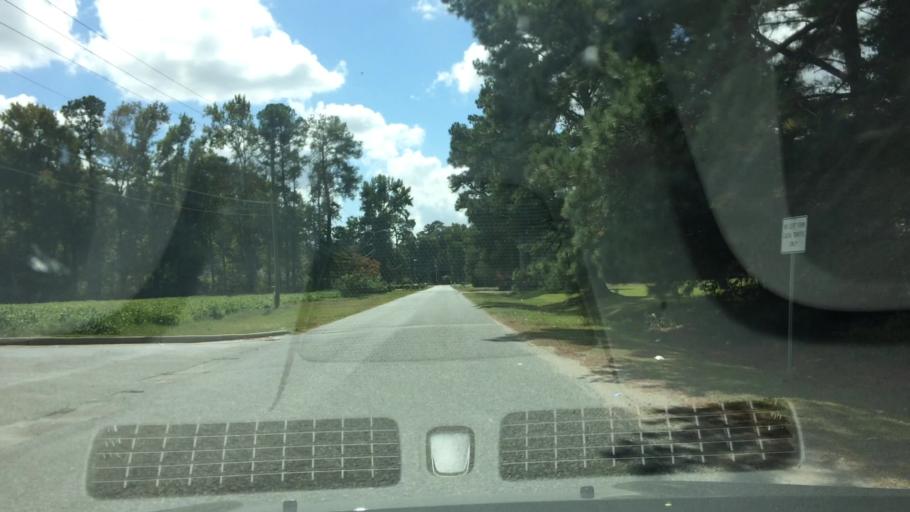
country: US
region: North Carolina
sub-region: Pitt County
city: Ayden
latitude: 35.4753
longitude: -77.4367
